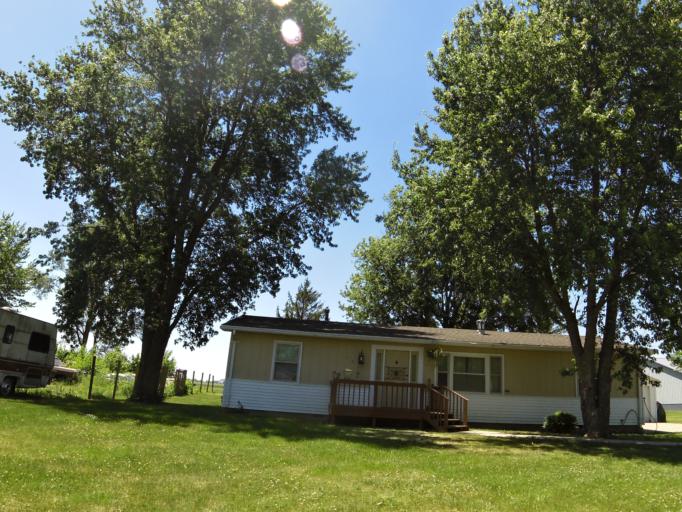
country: US
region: Illinois
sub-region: Livingston County
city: Chatsworth
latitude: 40.7542
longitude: -88.1917
